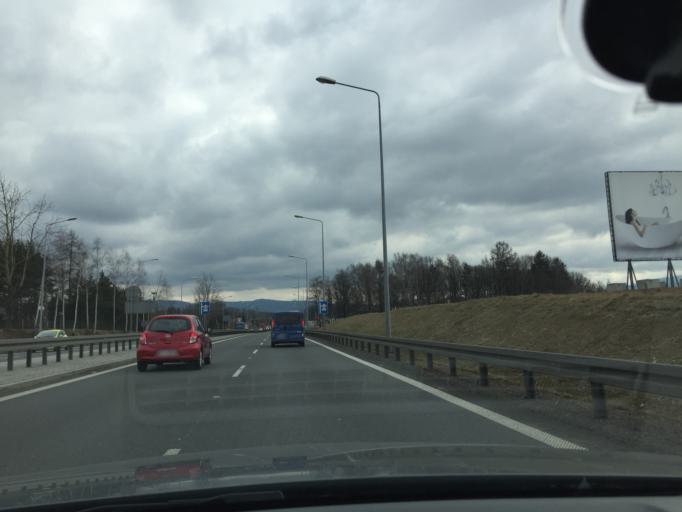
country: PL
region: Silesian Voivodeship
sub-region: Powiat bielski
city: Mazancowice
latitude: 49.8705
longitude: 19.0060
